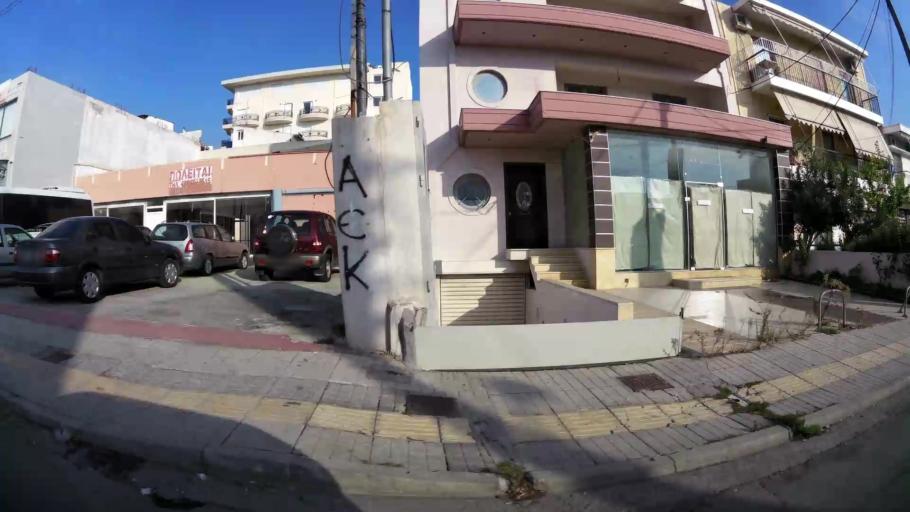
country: GR
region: Attica
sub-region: Nomarchia Anatolikis Attikis
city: Acharnes
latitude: 38.0835
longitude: 23.7303
